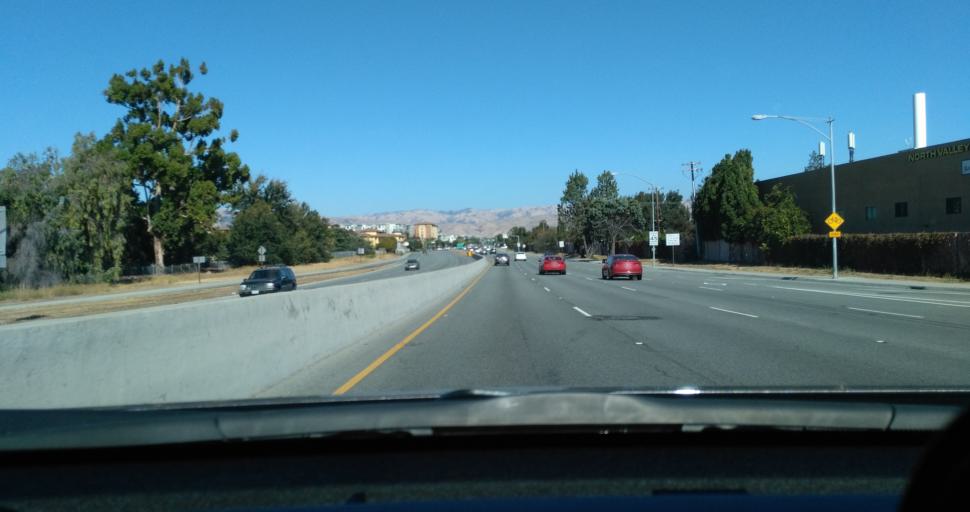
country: US
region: California
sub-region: Santa Clara County
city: Santa Clara
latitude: 37.3905
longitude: -121.9524
